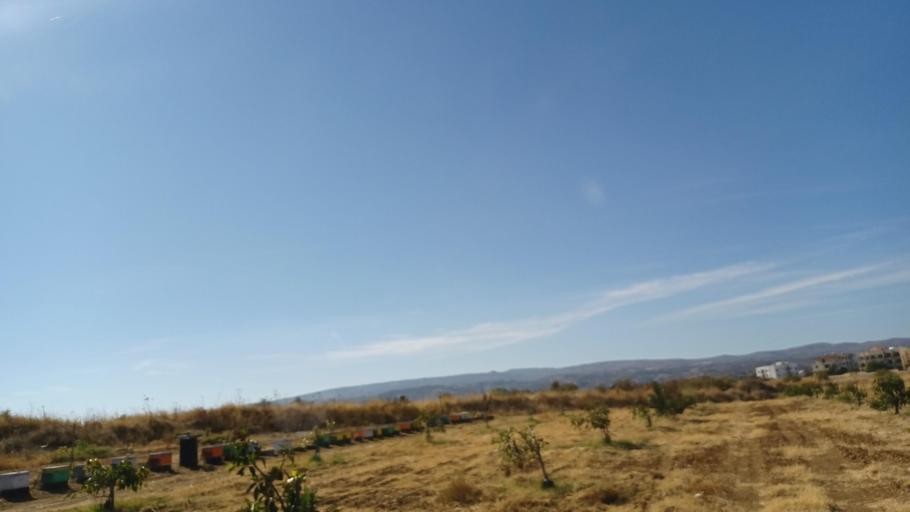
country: CY
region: Pafos
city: Polis
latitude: 35.0408
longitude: 32.4416
